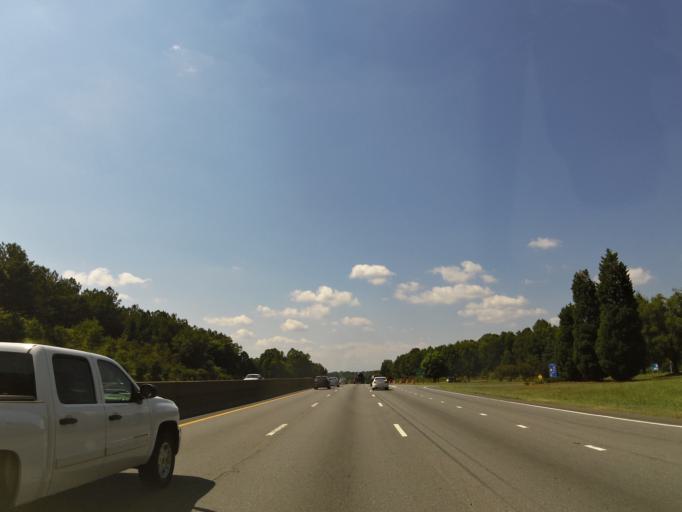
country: US
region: North Carolina
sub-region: Gaston County
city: Belmont
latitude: 35.2578
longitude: -81.0445
